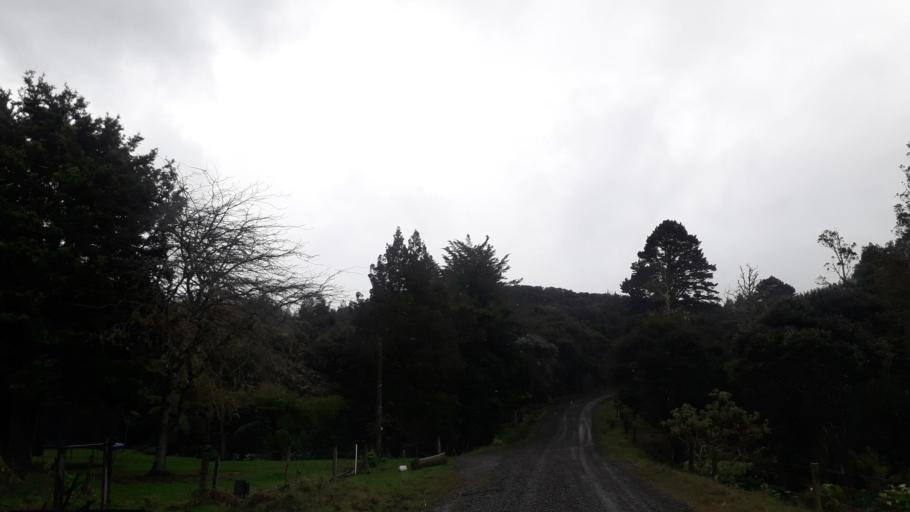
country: NZ
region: Northland
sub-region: Far North District
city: Kaitaia
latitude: -35.3925
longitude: 173.4043
